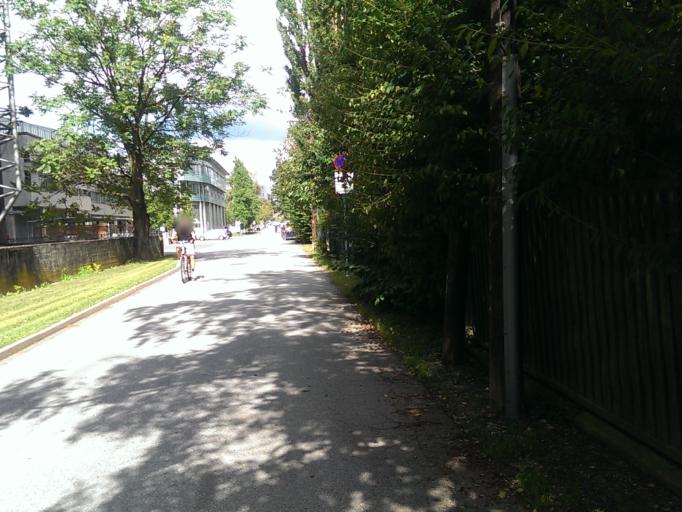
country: AT
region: Styria
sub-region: Graz Stadt
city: Graz
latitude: 47.0576
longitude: 15.4585
